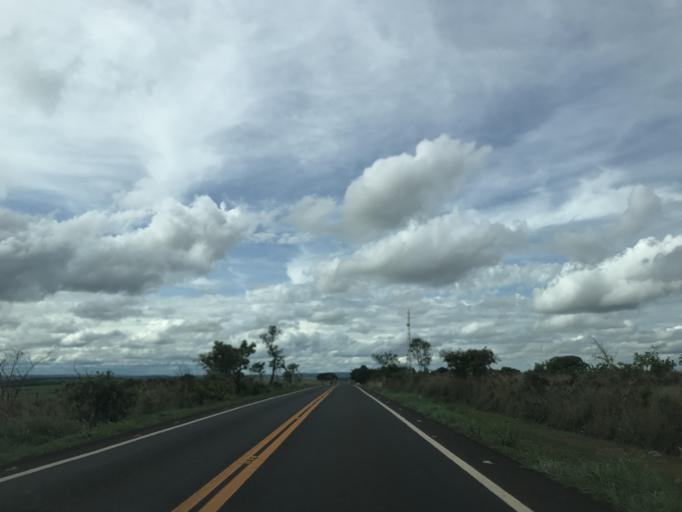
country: BR
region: Goias
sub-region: Piracanjuba
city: Piracanjuba
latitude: -17.4268
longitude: -48.8043
